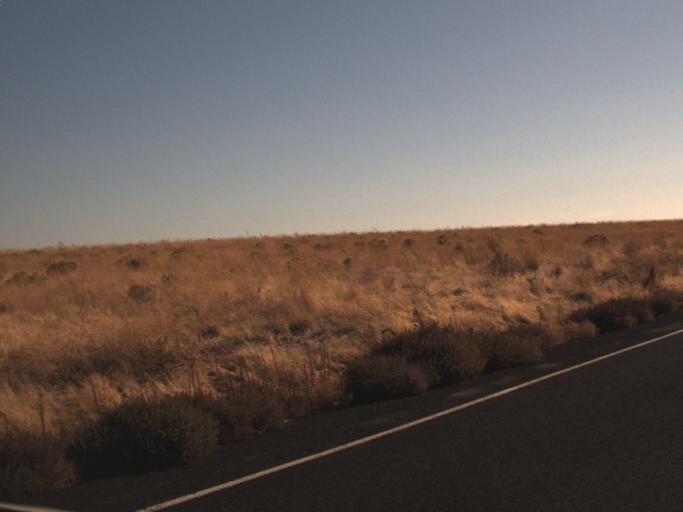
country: US
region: Washington
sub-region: Adams County
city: Ritzville
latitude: 47.0557
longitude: -118.6630
